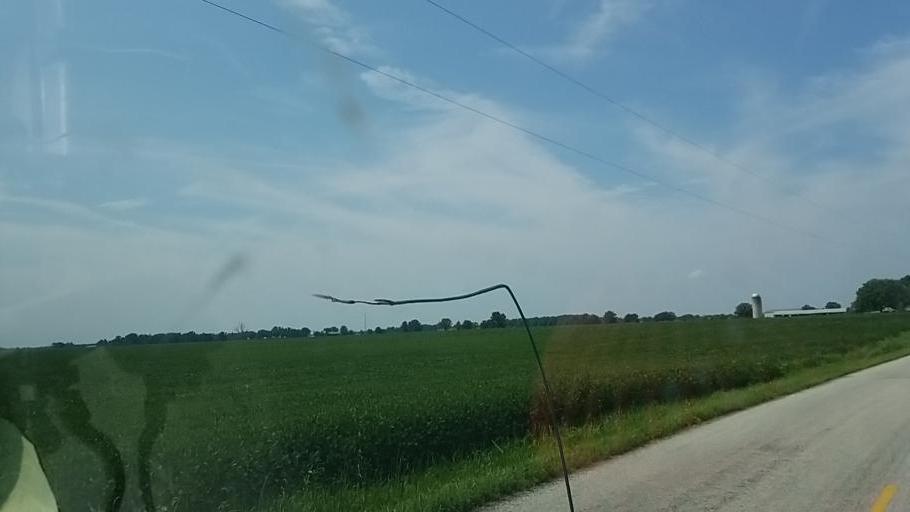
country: US
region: Ohio
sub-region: Marion County
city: Marion
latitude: 40.5973
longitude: -83.0519
